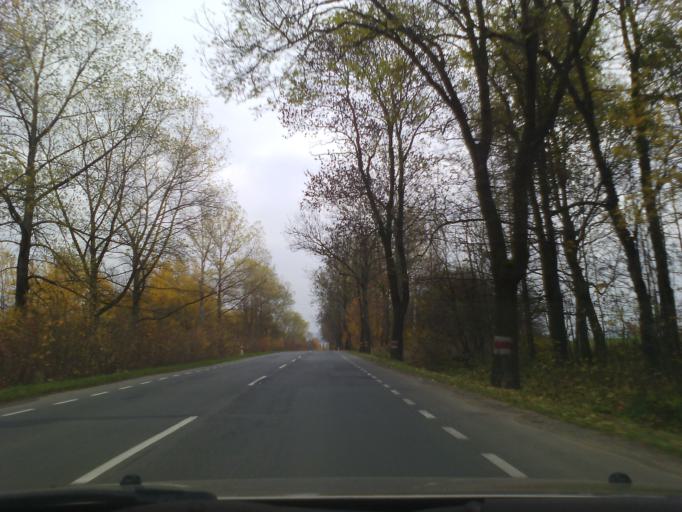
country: PL
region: Lower Silesian Voivodeship
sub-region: Powiat walbrzyski
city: Czarny Bor
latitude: 50.7825
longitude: 16.0941
